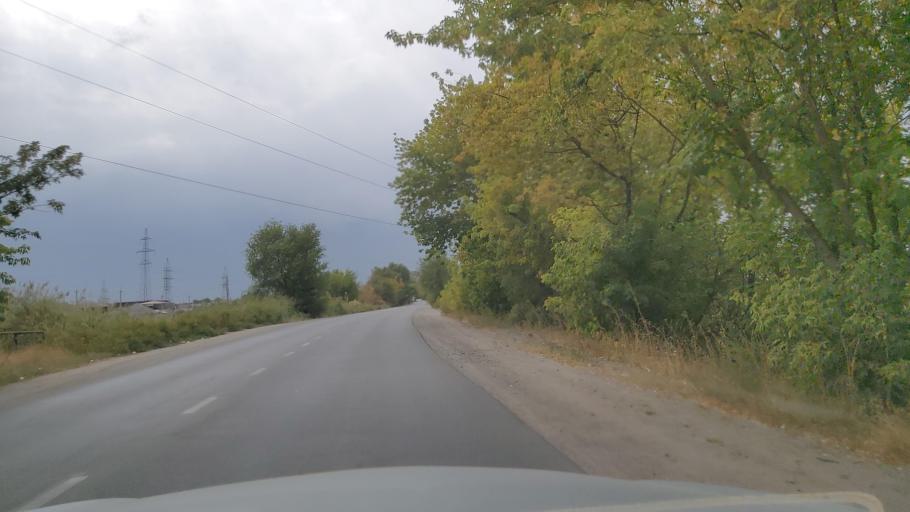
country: KZ
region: Almaty Oblysy
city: Energeticheskiy
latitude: 43.4031
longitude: 77.0342
